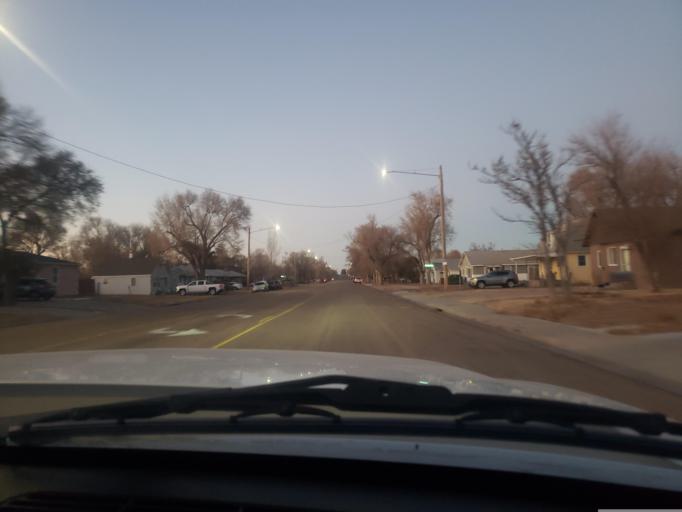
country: US
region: Kansas
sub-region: Finney County
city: Garden City
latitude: 37.9853
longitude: -100.8693
